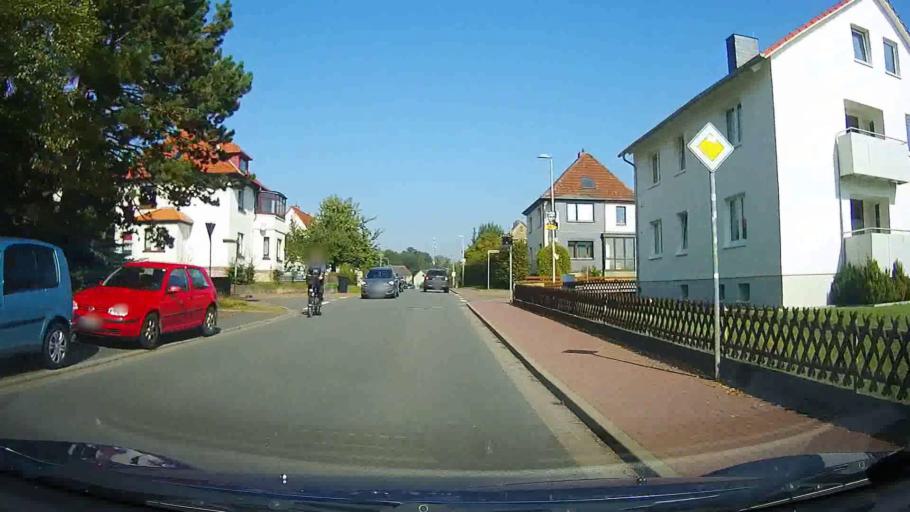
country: DE
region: Lower Saxony
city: Moringen
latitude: 51.7017
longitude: 9.8759
